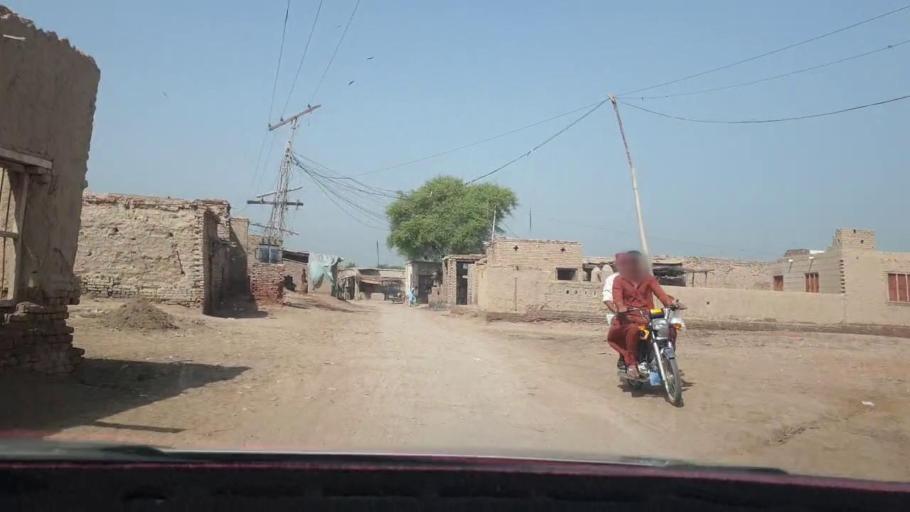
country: PK
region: Sindh
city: Nasirabad
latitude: 27.4254
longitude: 67.9260
